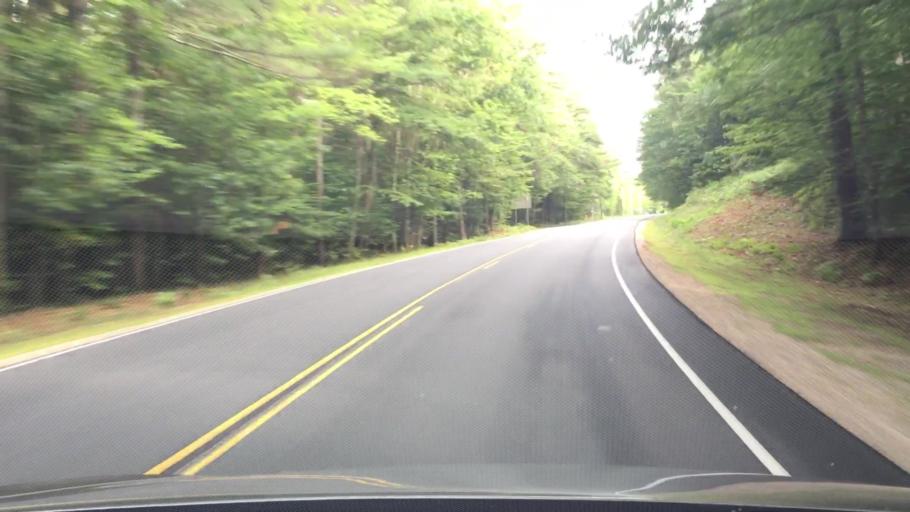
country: US
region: New Hampshire
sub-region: Carroll County
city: Conway
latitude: 43.9848
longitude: -71.1417
